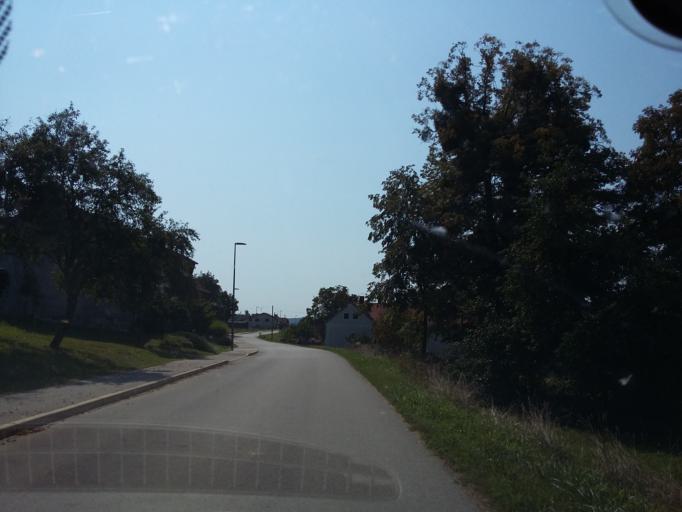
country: SI
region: Salovci
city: Salovci
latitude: 46.8349
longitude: 16.3166
